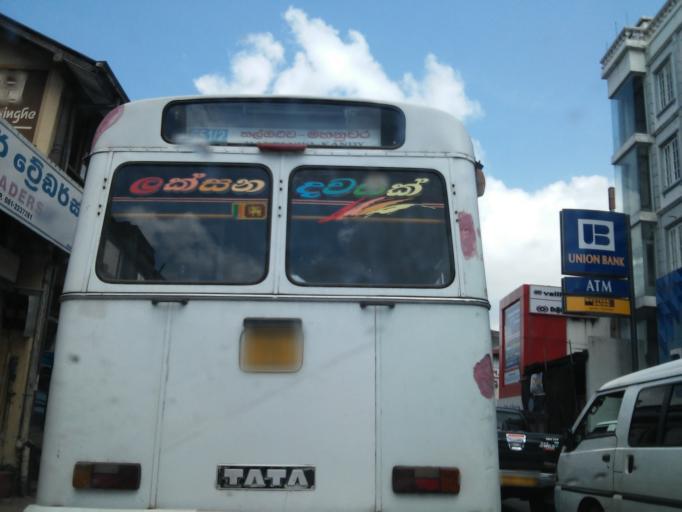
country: LK
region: Central
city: Kandy
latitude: 7.2978
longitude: 80.6372
